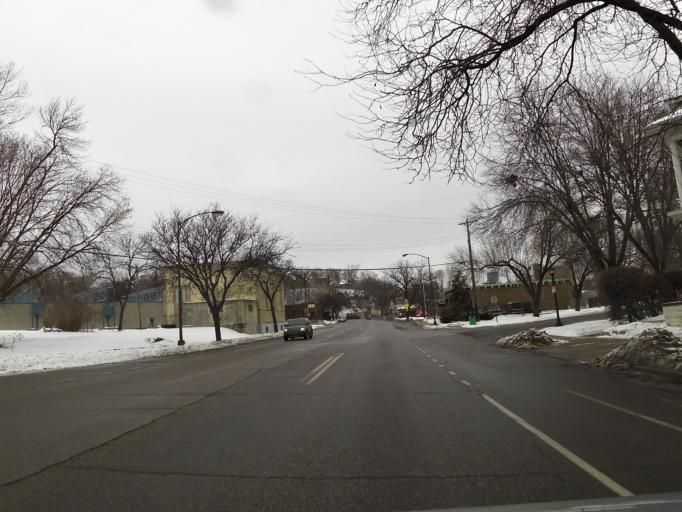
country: US
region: Minnesota
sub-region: Ramsey County
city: Saint Paul
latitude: 44.9324
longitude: -93.0820
